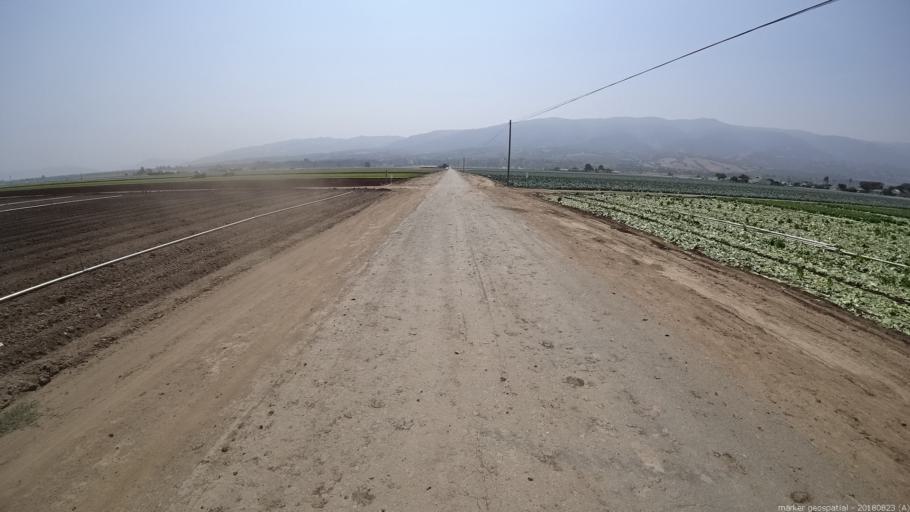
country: US
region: California
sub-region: Monterey County
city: Soledad
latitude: 36.3990
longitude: -121.3419
